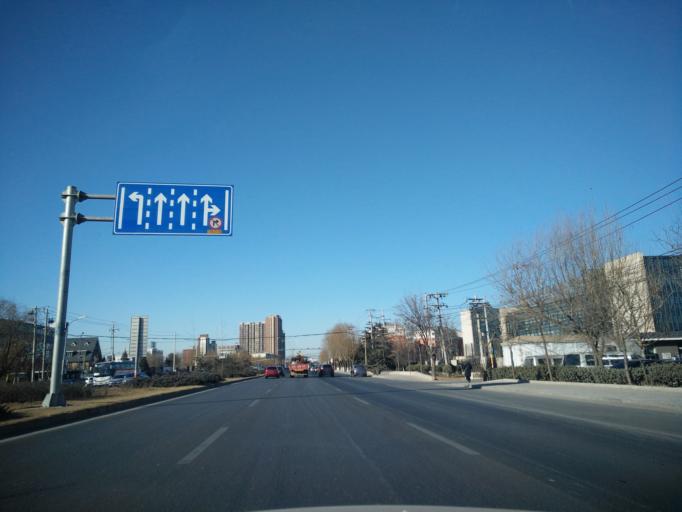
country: CN
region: Beijing
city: Xingfeng
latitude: 39.7205
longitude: 116.3497
